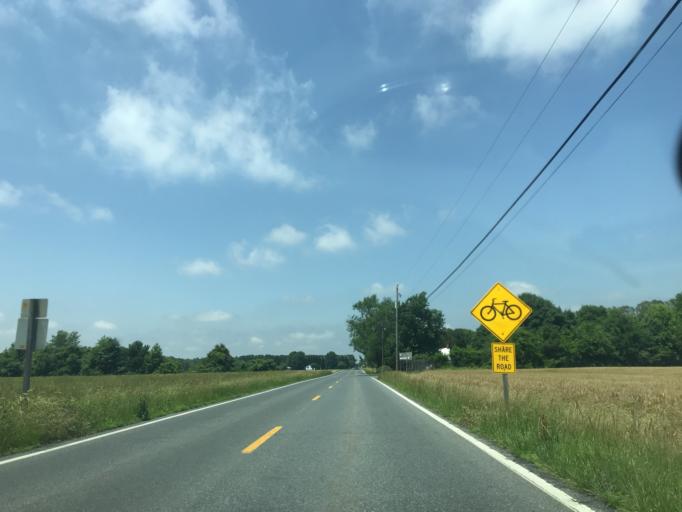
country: US
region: Maryland
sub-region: Dorchester County
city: Hurlock
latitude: 38.5945
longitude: -75.9516
